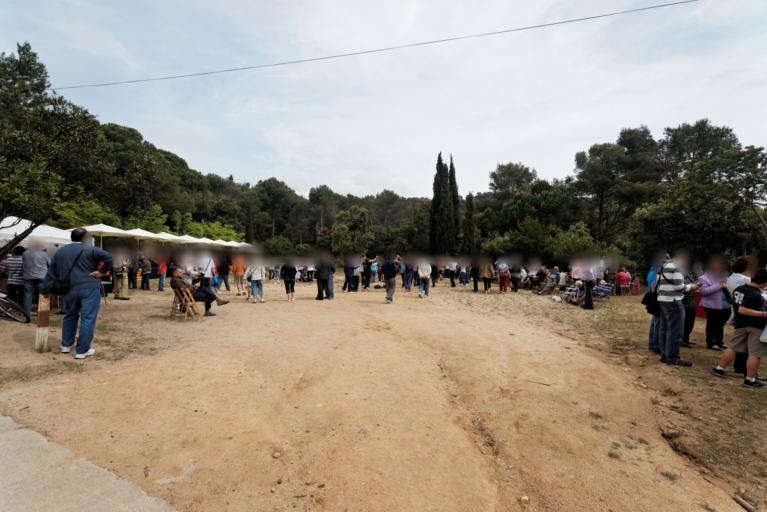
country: ES
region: Catalonia
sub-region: Provincia de Girona
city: Blanes
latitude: 41.6888
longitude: 2.8147
